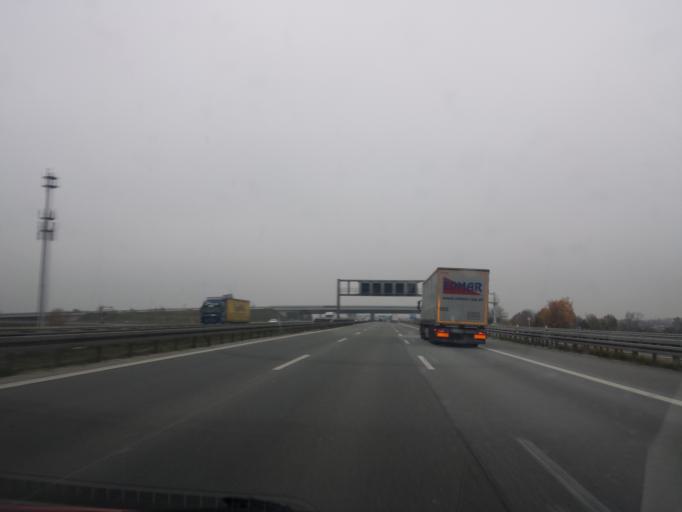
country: DE
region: Bavaria
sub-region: Upper Bavaria
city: Eching
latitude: 48.3203
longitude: 11.6185
